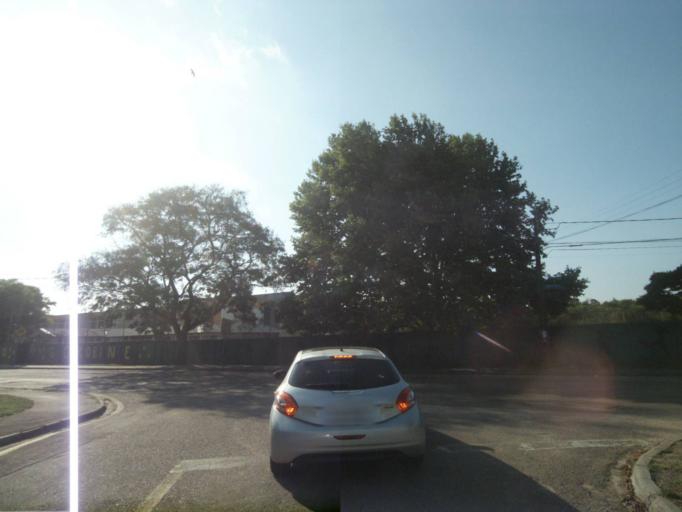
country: BR
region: Parana
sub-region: Curitiba
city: Curitiba
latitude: -25.4804
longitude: -49.3307
